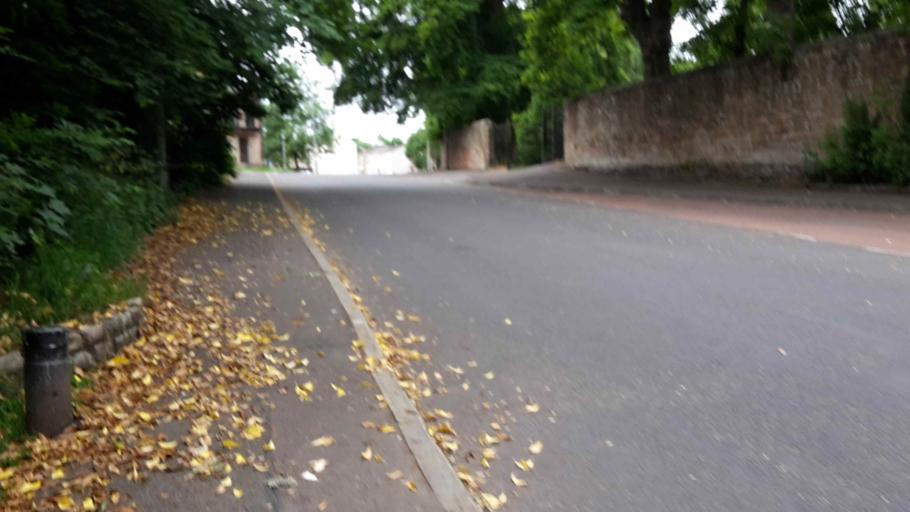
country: GB
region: Scotland
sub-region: South Lanarkshire
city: Bothwell
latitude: 55.8015
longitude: -4.0834
